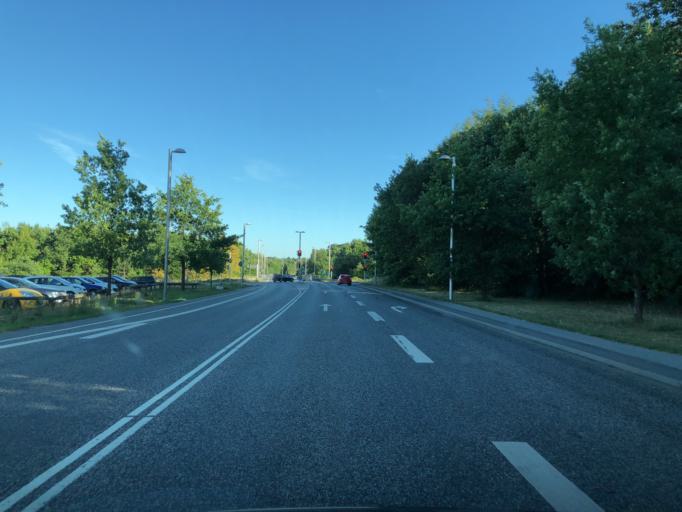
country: DK
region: Central Jutland
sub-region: Skanderborg Kommune
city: Stilling
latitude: 56.0683
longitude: 9.9765
